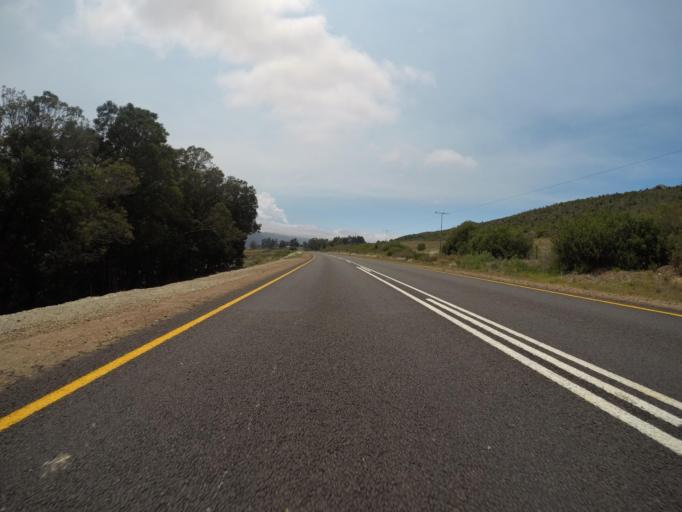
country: ZA
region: Western Cape
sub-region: Eden District Municipality
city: Knysna
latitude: -33.7748
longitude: 22.9085
